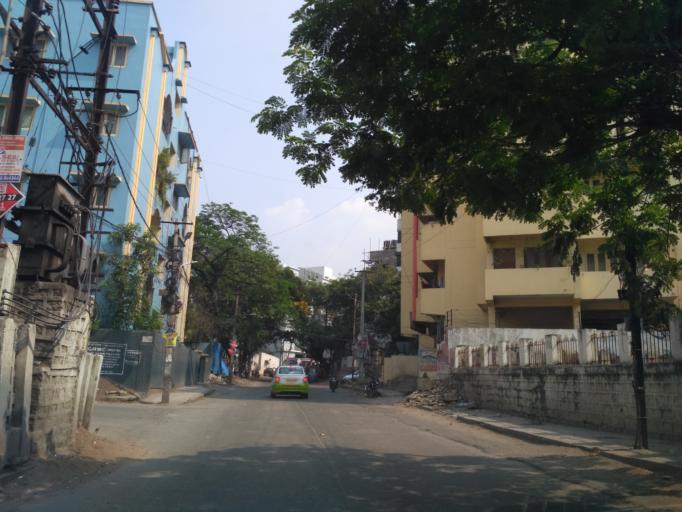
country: IN
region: Telangana
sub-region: Hyderabad
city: Hyderabad
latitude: 17.4314
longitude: 78.4385
